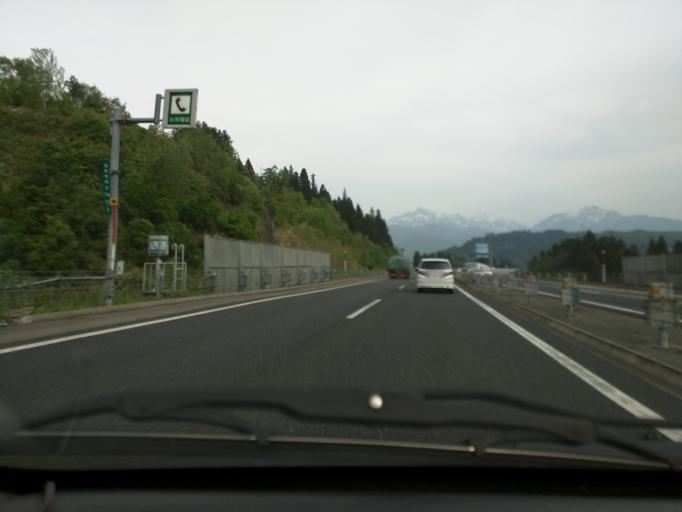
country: JP
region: Niigata
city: Ojiya
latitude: 37.2504
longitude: 138.9347
